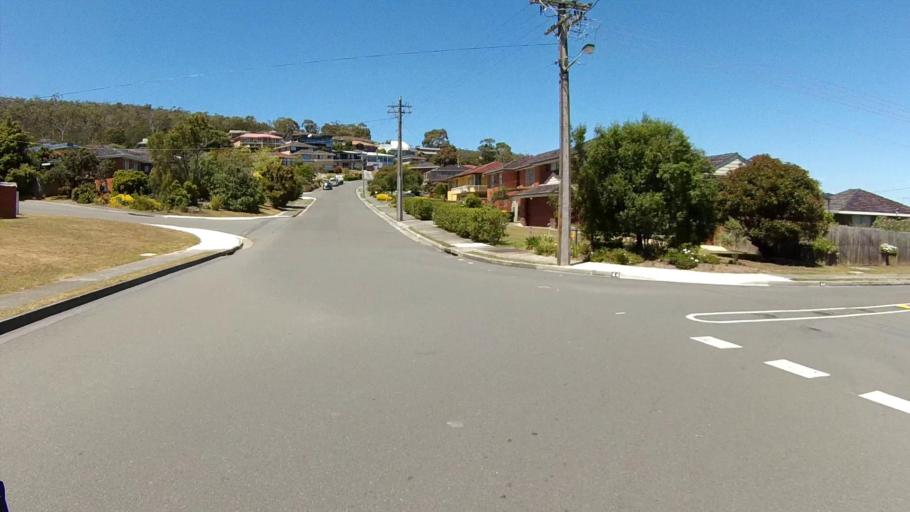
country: AU
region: Tasmania
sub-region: Clarence
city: Howrah
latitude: -42.8772
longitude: 147.4093
